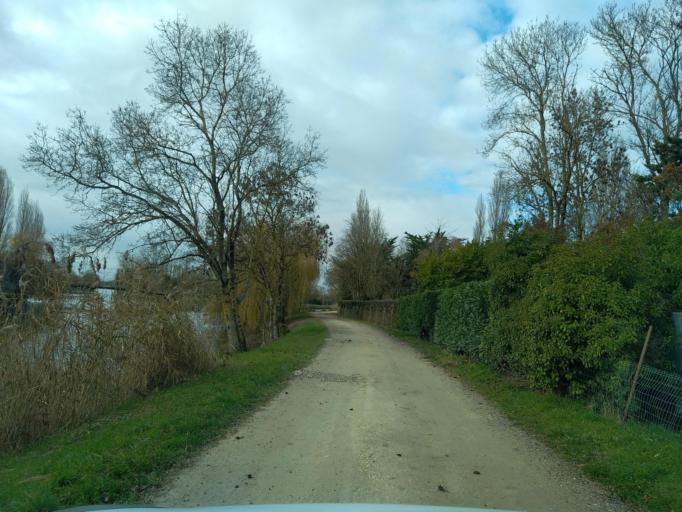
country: FR
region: Pays de la Loire
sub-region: Departement de la Vendee
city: Maillezais
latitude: 46.3138
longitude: -0.7713
